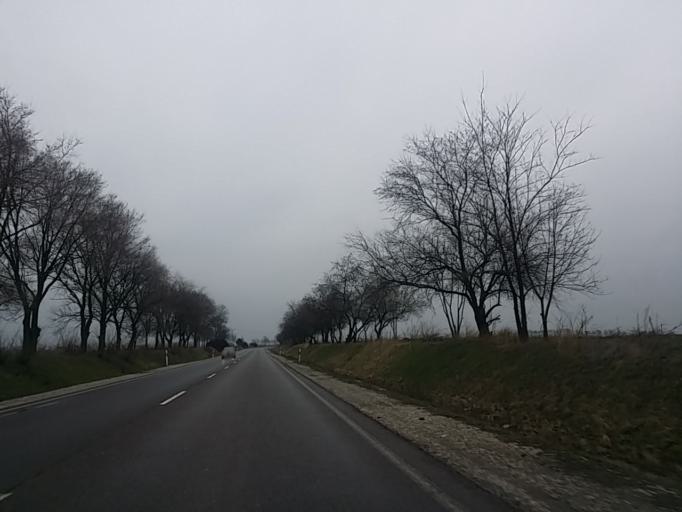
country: HU
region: Borsod-Abauj-Zemplen
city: Mezokovesd
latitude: 47.8038
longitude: 20.5410
